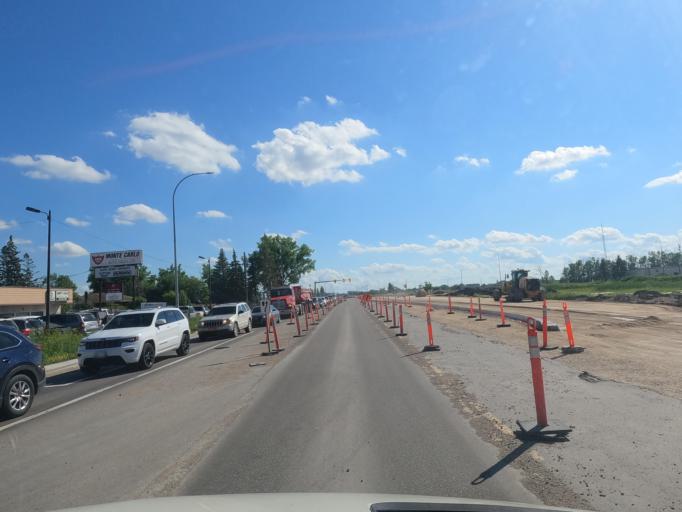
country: CA
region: Manitoba
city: Winnipeg
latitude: 49.9780
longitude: -97.0688
